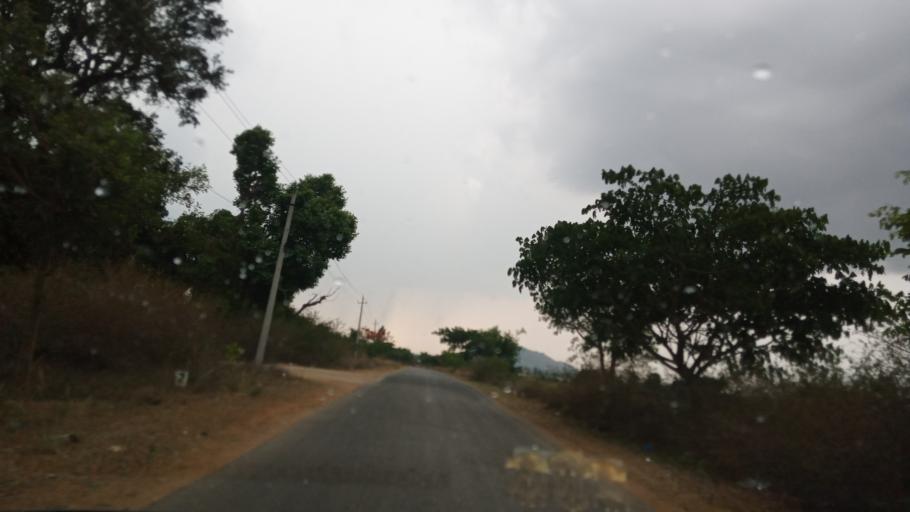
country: IN
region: Karnataka
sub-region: Kolar
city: Mulbagal
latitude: 13.1350
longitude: 78.3585
